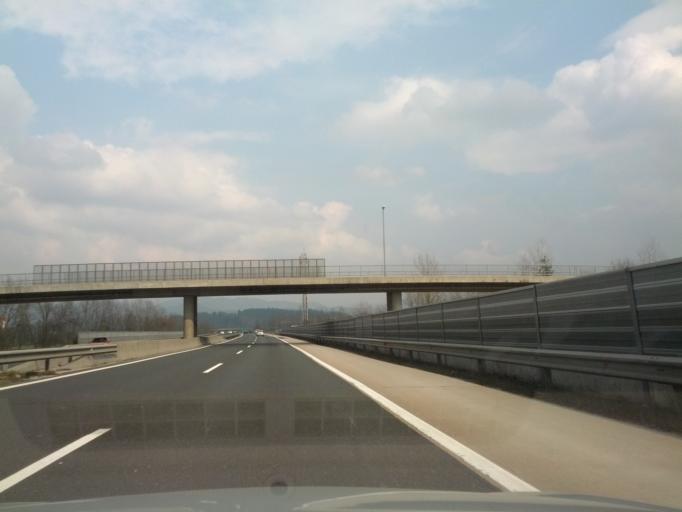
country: SI
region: Domzale
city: Dob
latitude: 46.1422
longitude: 14.6314
